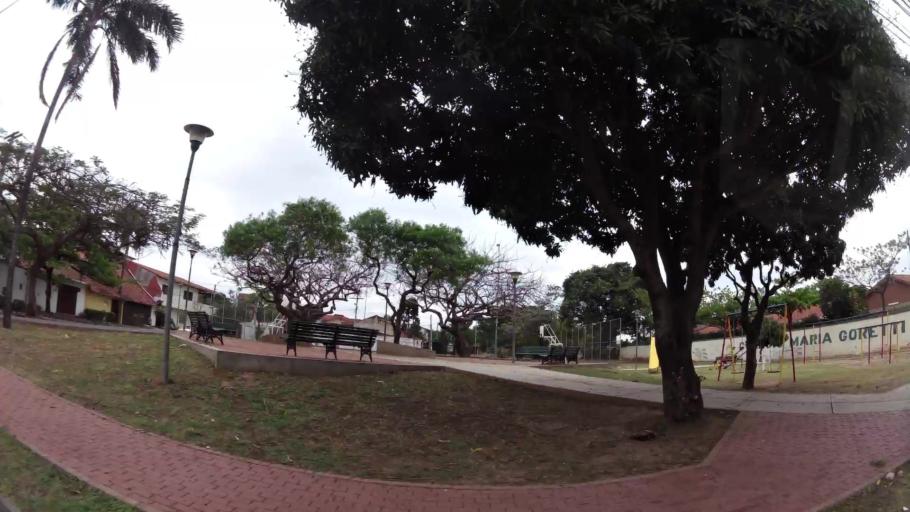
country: BO
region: Santa Cruz
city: Santa Cruz de la Sierra
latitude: -17.7651
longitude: -63.1649
